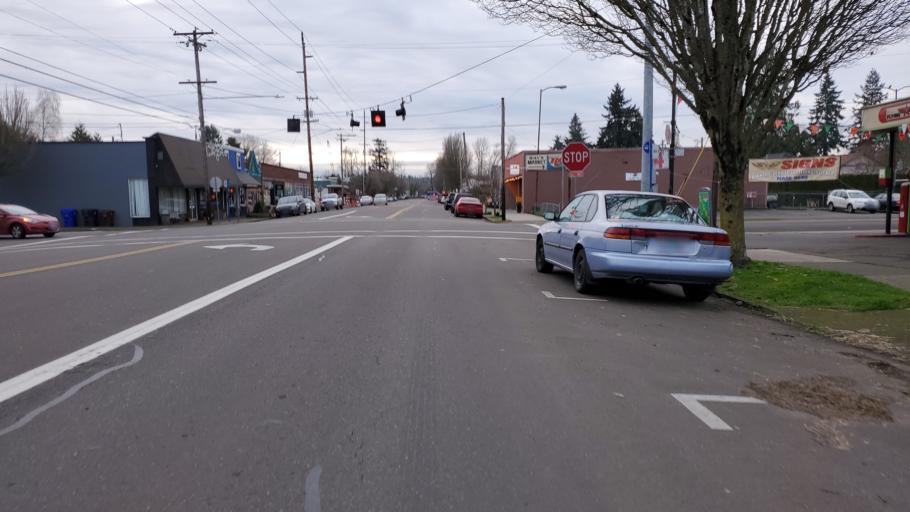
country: US
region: Oregon
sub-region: Clackamas County
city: Gladstone
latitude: 45.3805
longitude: -122.5948
